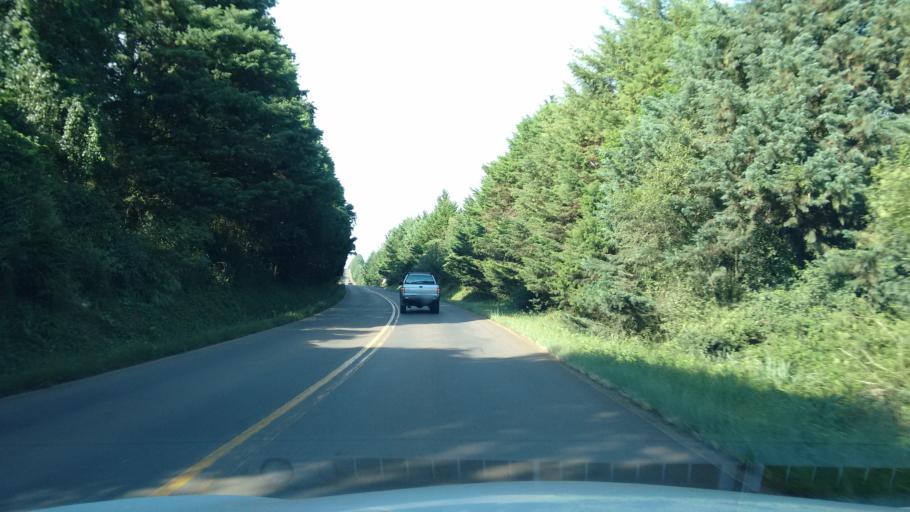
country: BR
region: Santa Catarina
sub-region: Videira
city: Videira
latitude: -27.1347
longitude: -50.9450
